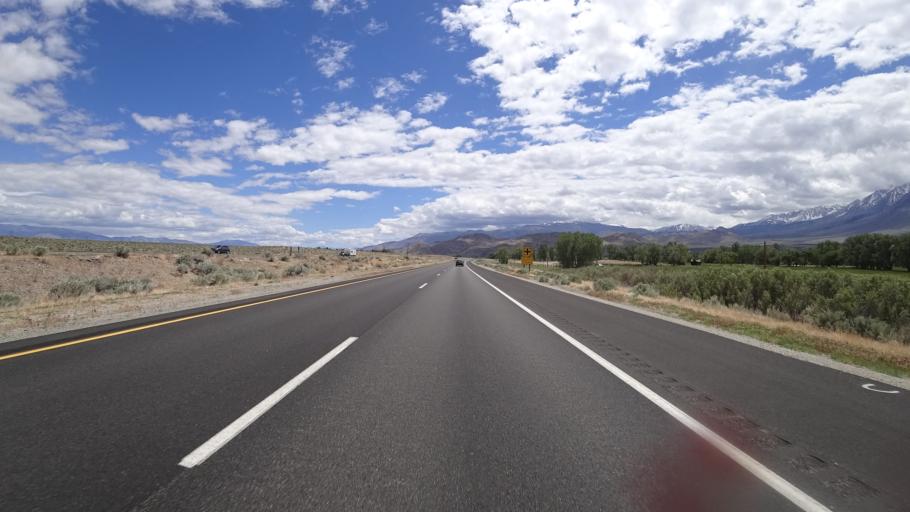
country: US
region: California
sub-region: Inyo County
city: West Bishop
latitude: 37.4229
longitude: -118.5577
